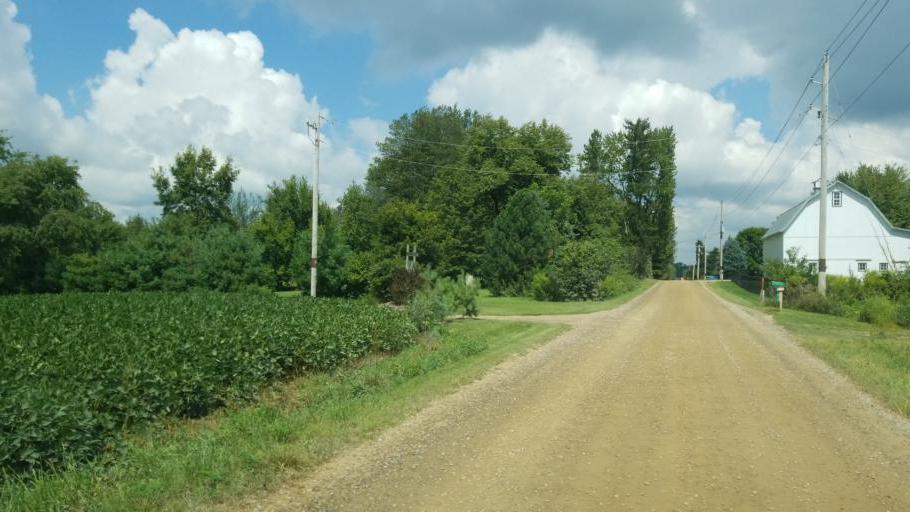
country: US
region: Ohio
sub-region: Knox County
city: Mount Vernon
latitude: 40.3197
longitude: -82.4925
